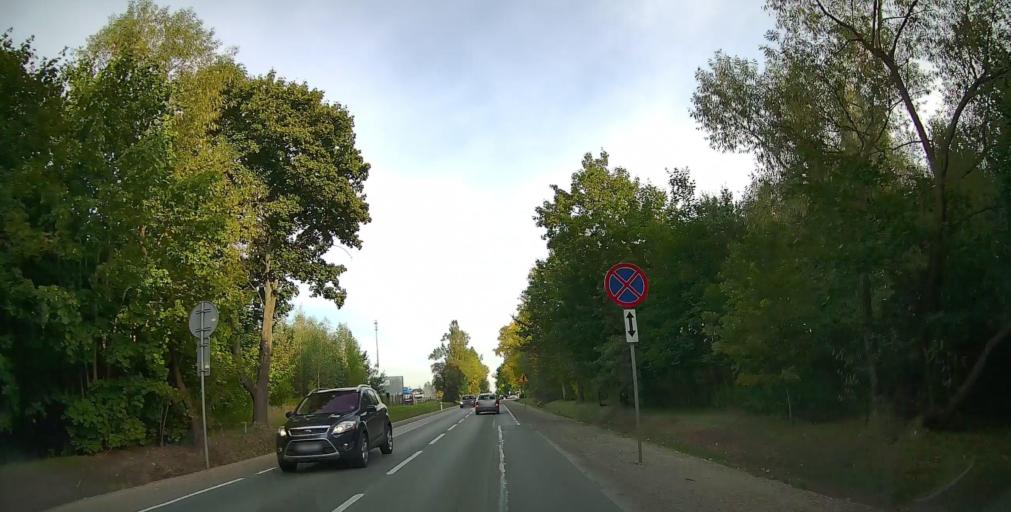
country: PL
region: Masovian Voivodeship
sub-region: Powiat piaseczynski
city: Zabieniec
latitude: 52.0566
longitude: 21.0520
